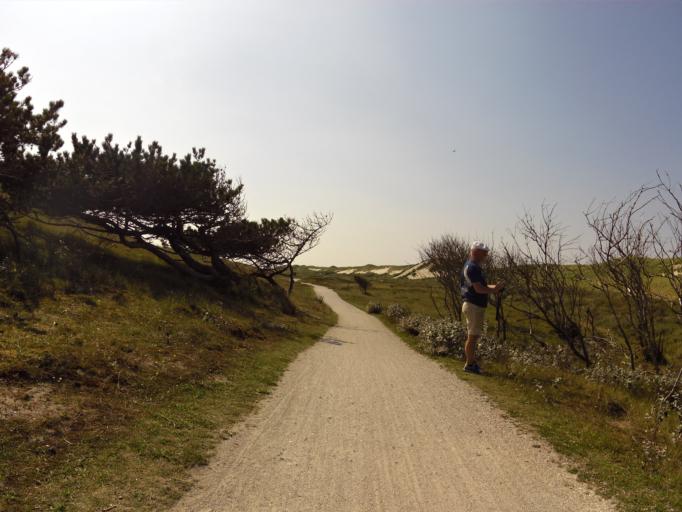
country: NL
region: North Holland
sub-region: Gemeente Schagen
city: Harenkarspel
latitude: 52.7882
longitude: 4.6720
